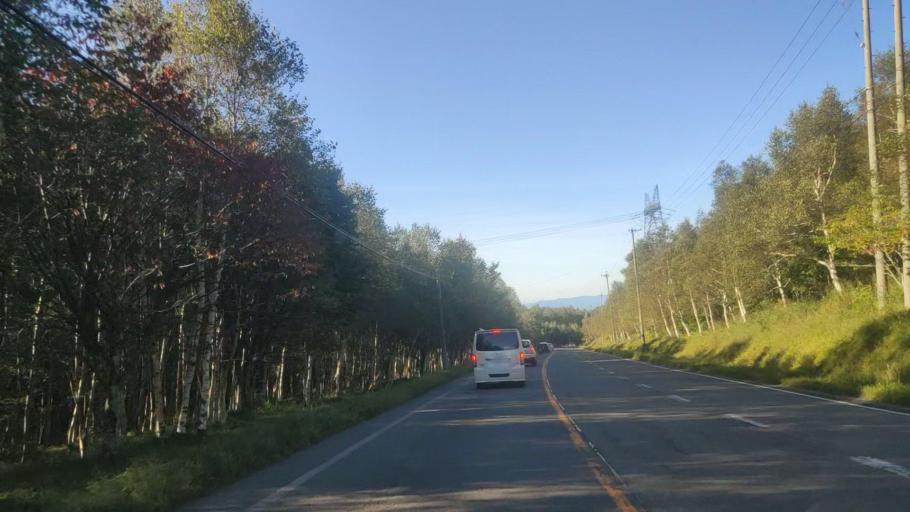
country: JP
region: Nagano
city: Kamimaruko
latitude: 36.1570
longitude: 138.2792
